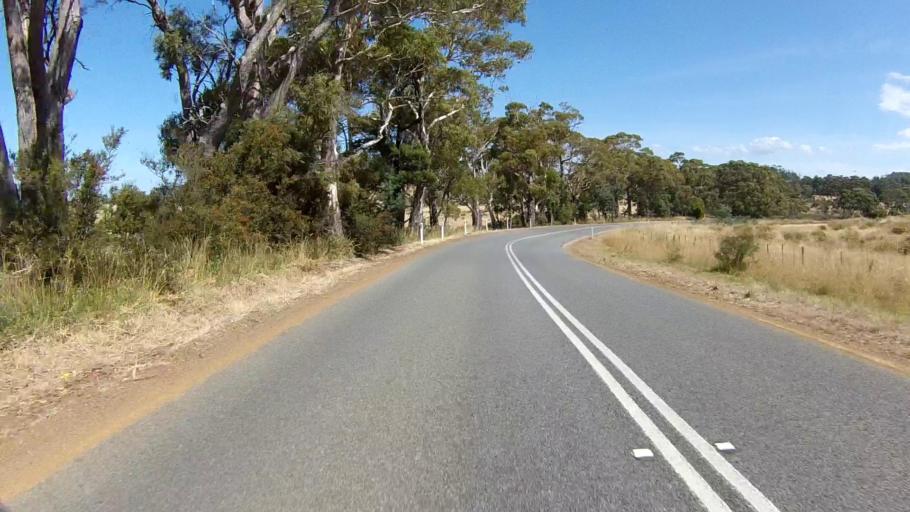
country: AU
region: Tasmania
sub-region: Sorell
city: Sorell
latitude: -42.3035
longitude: 147.9702
